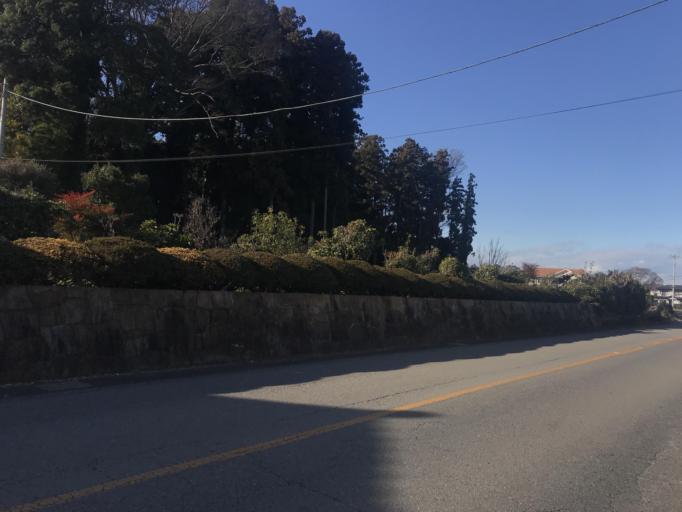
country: JP
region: Tochigi
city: Kaminokawa
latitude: 36.4165
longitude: 139.8776
